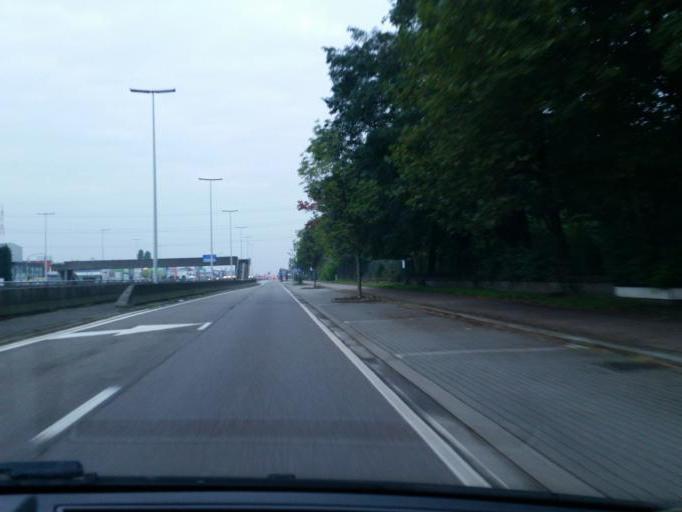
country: BE
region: Flanders
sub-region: Provincie Antwerpen
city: Boom
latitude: 51.1117
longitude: 4.3713
